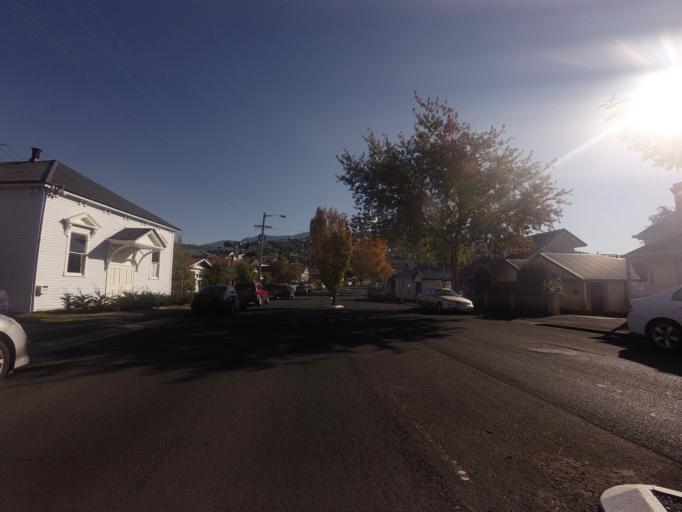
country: AU
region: Tasmania
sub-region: Hobart
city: Sandy Bay
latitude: -42.8841
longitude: 147.3138
